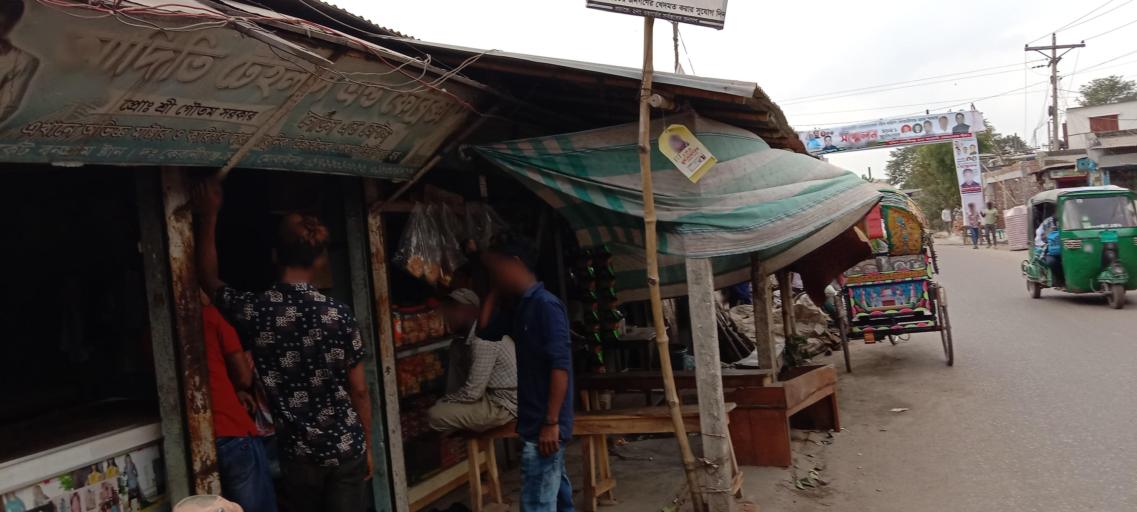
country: BD
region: Dhaka
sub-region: Dhaka
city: Dhaka
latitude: 23.6598
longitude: 90.4143
